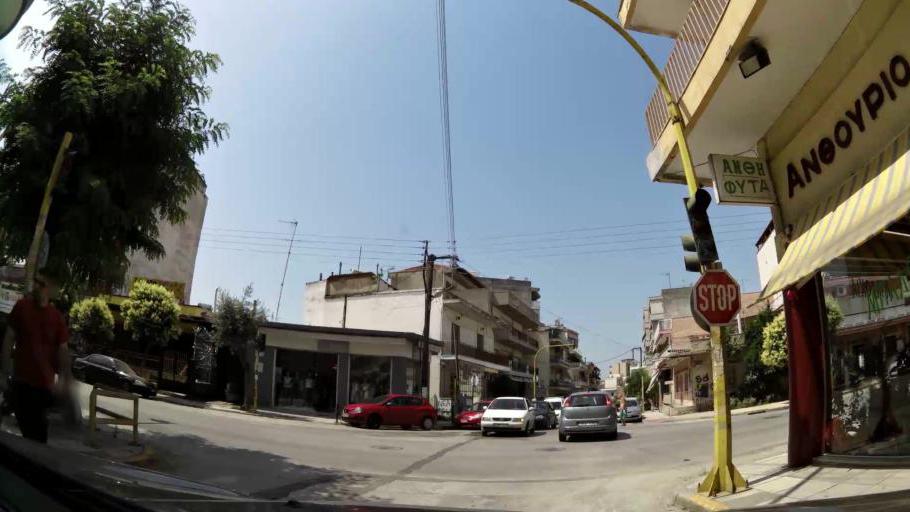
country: GR
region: Central Macedonia
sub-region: Nomos Thessalonikis
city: Evosmos
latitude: 40.6680
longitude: 22.9134
